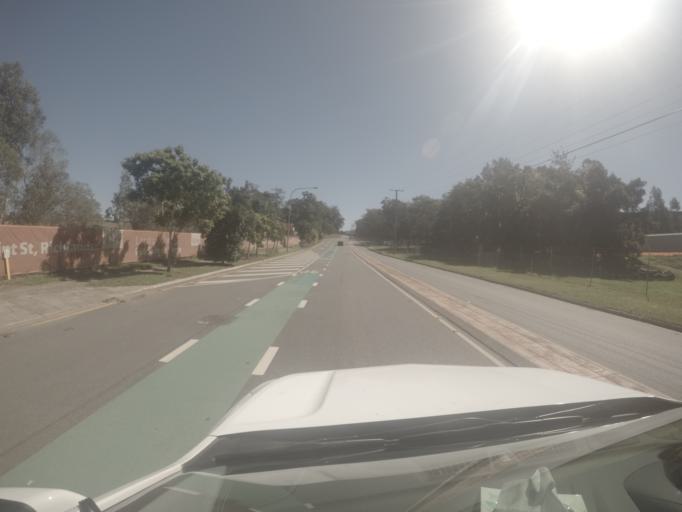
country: AU
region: Queensland
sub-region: Brisbane
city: Inala
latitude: -27.5732
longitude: 152.9700
